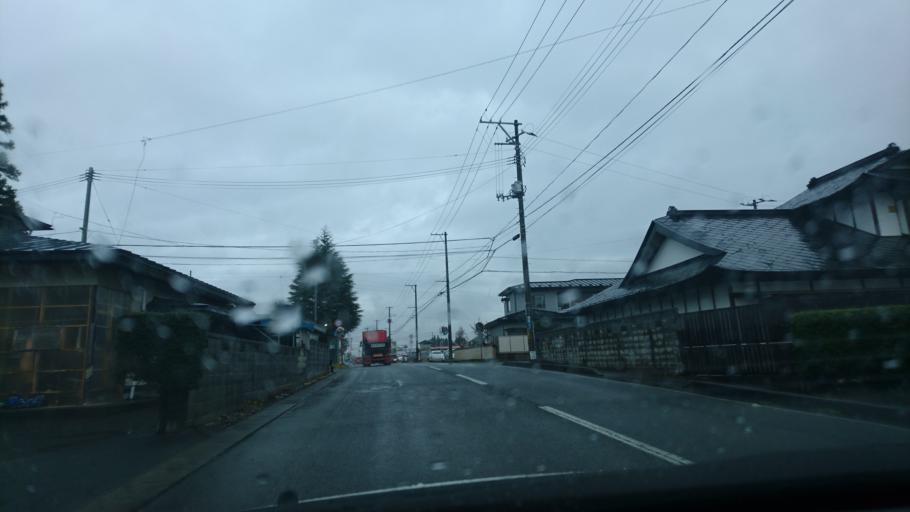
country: JP
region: Iwate
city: Kitakami
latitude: 39.2951
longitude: 141.0548
